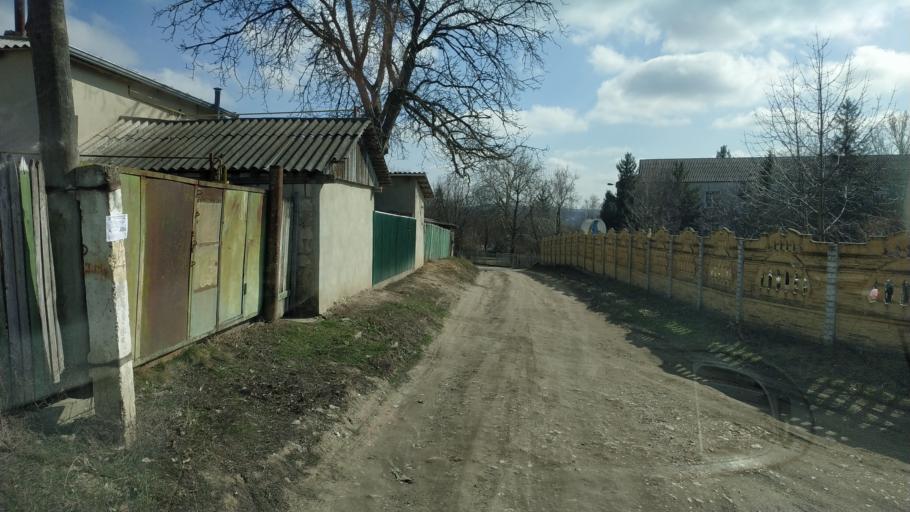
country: MD
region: Hincesti
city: Hincesti
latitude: 46.8281
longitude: 28.6700
